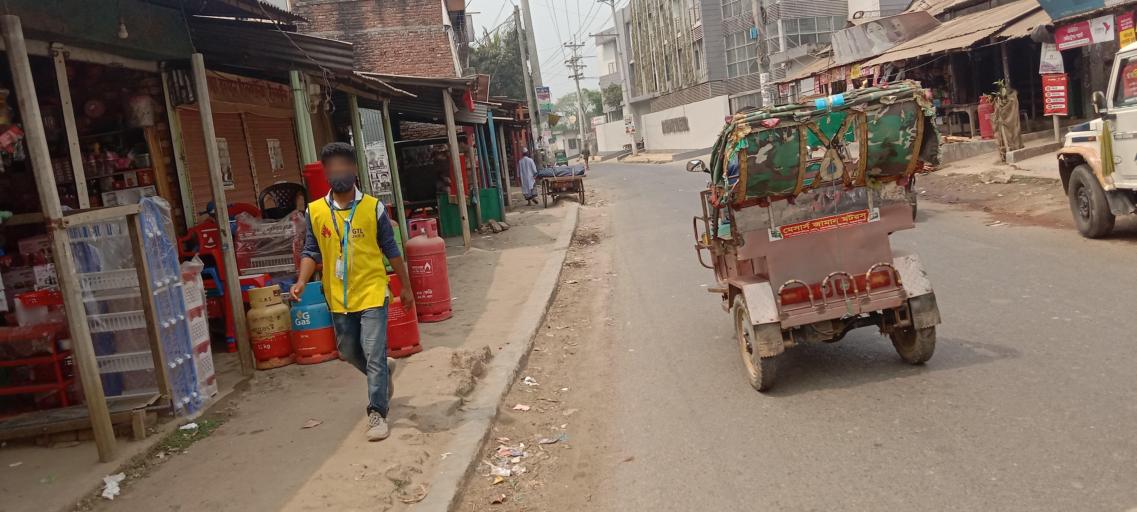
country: BD
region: Dhaka
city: Sakhipur
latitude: 24.4450
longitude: 90.3392
